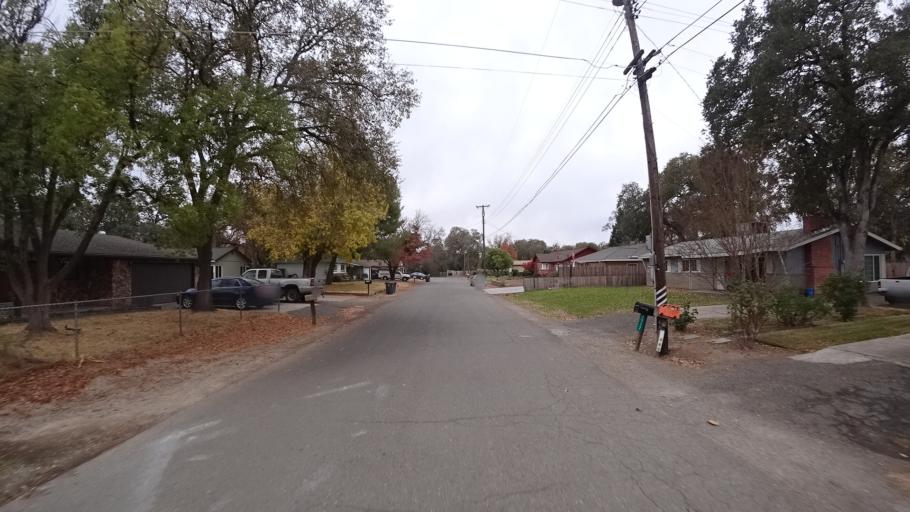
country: US
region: California
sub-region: Sacramento County
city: Citrus Heights
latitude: 38.7068
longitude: -121.2944
